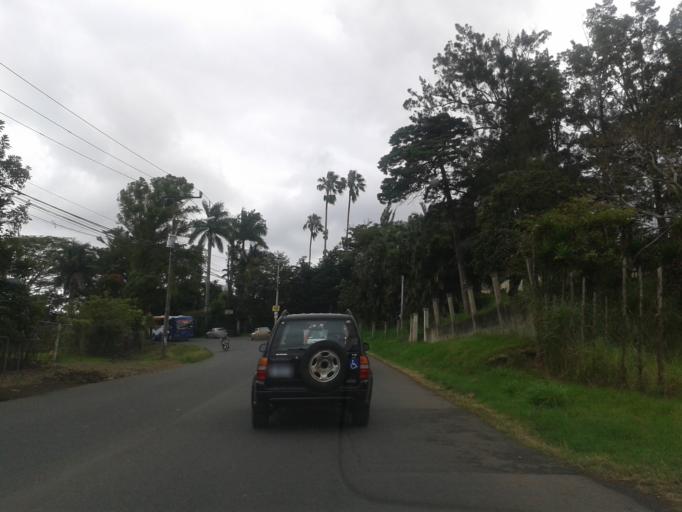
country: CR
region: San Jose
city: San Rafael Arriba
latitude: 9.8843
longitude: -84.0684
